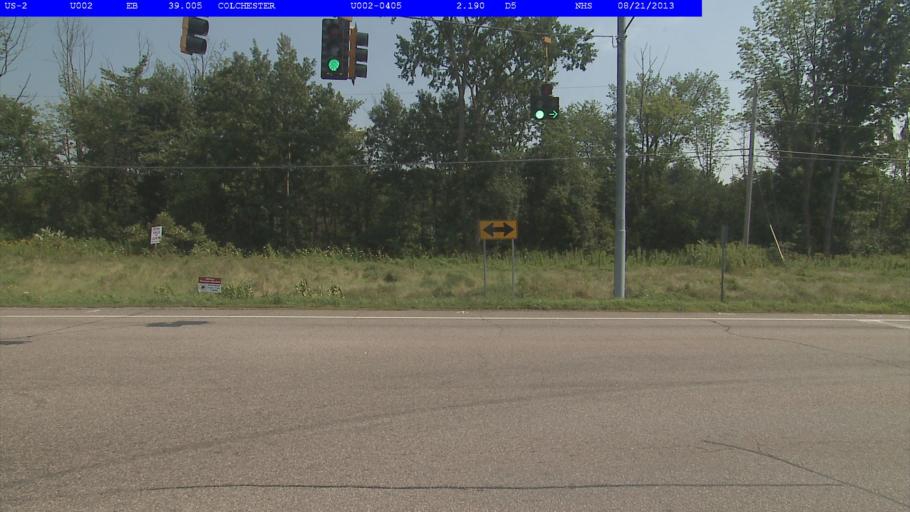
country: US
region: Vermont
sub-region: Chittenden County
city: Colchester
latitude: 44.5895
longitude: -73.1666
